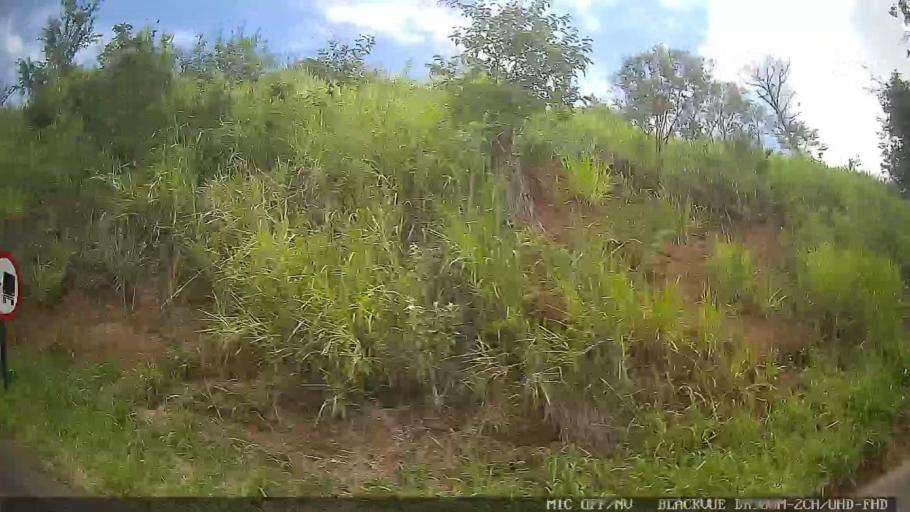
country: BR
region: Sao Paulo
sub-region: Tiete
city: Tiete
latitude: -23.1075
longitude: -47.7621
